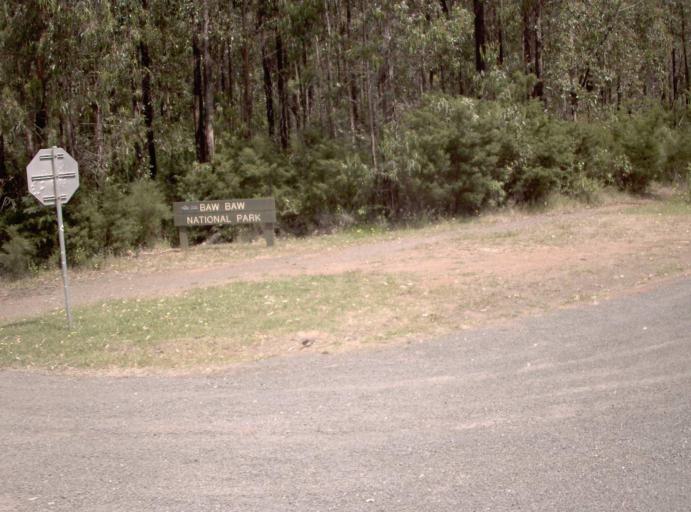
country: AU
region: Victoria
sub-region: Latrobe
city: Moe
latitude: -37.9272
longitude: 146.4013
